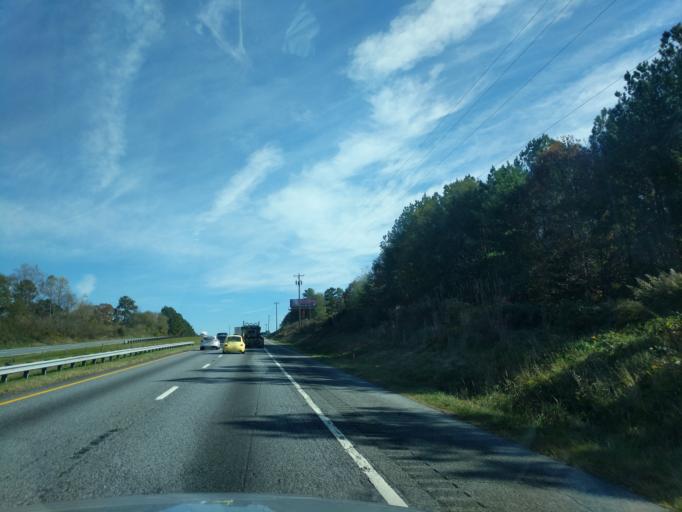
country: US
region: South Carolina
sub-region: Spartanburg County
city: Cowpens
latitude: 35.0346
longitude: -81.8427
